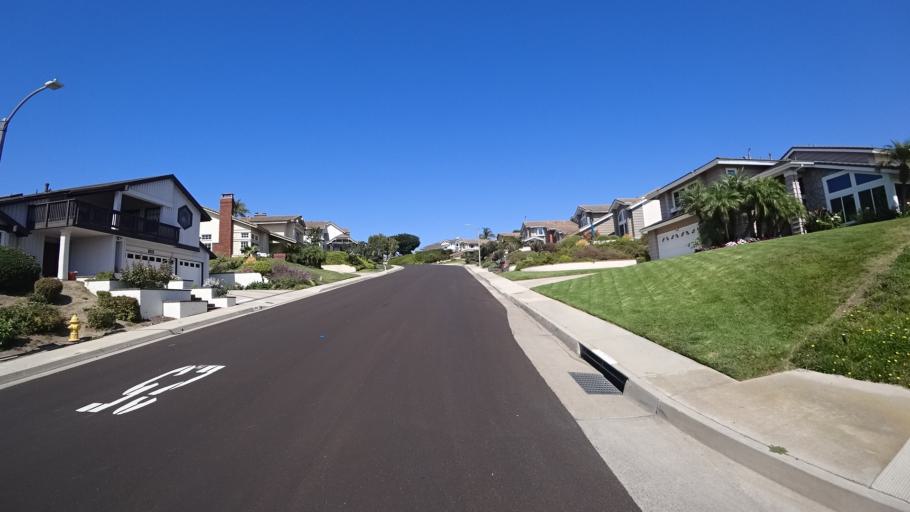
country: US
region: California
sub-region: Orange County
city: San Clemente
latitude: 33.4527
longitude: -117.6345
